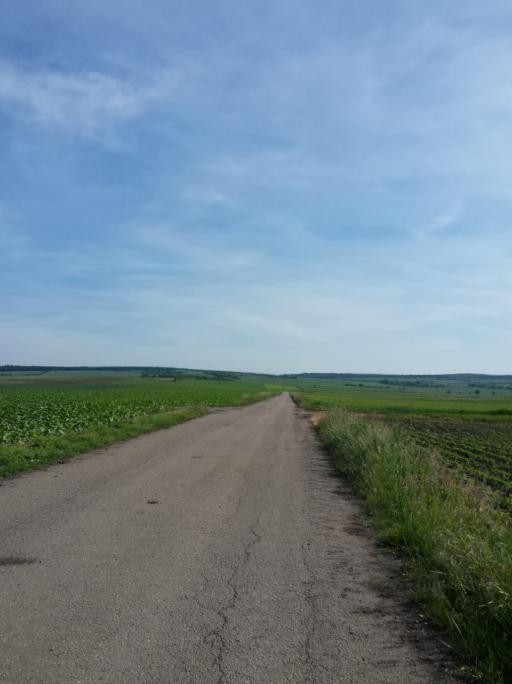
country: AT
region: Lower Austria
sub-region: Politischer Bezirk Hollabrunn
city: Wullersdorf
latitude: 48.6372
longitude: 16.1055
